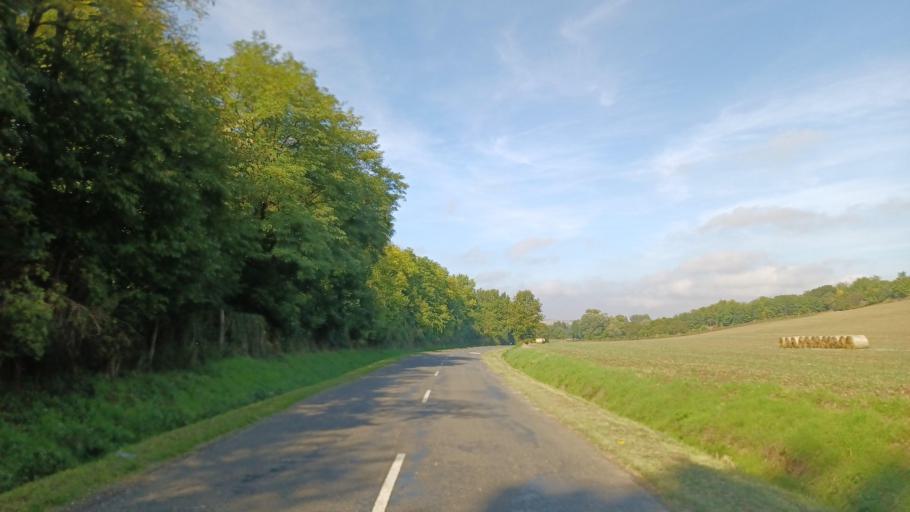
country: HU
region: Tolna
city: Pincehely
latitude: 46.6875
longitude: 18.4601
